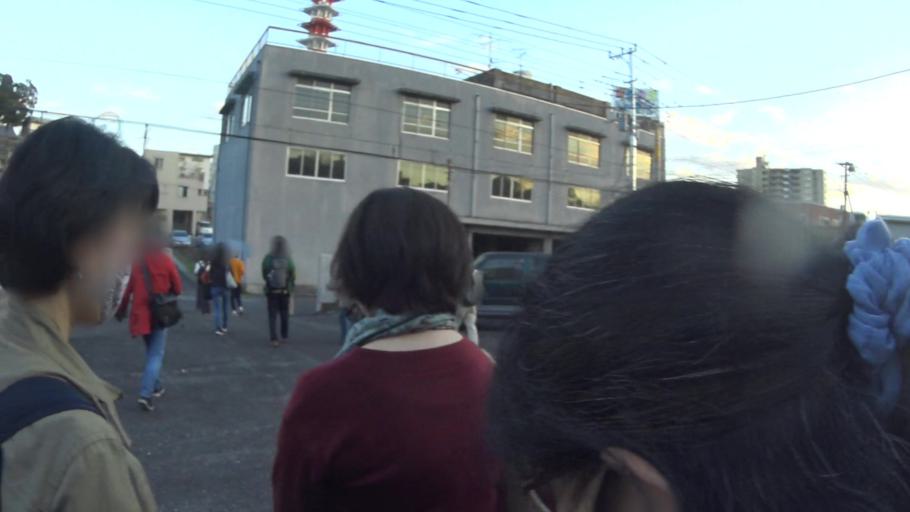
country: JP
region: Ibaraki
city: Mito-shi
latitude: 36.3725
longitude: 140.4719
